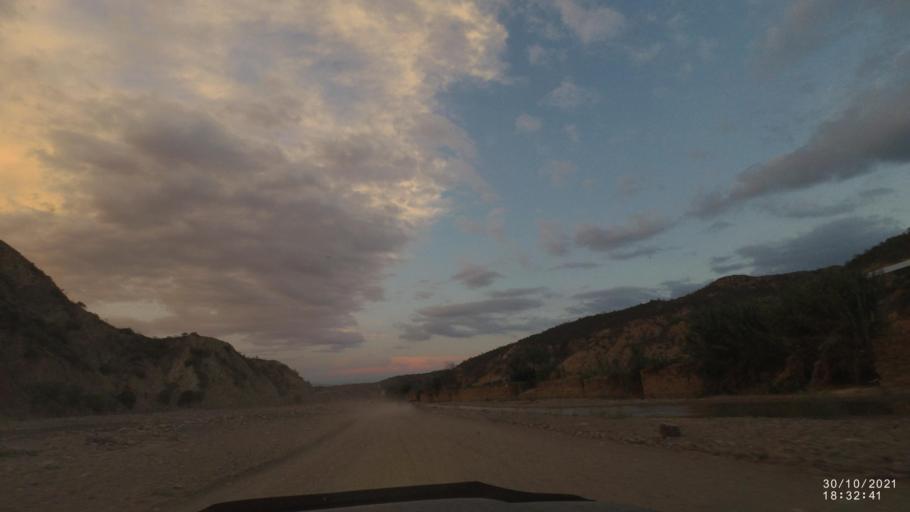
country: BO
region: Cochabamba
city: Sipe Sipe
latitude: -17.5655
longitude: -66.3744
